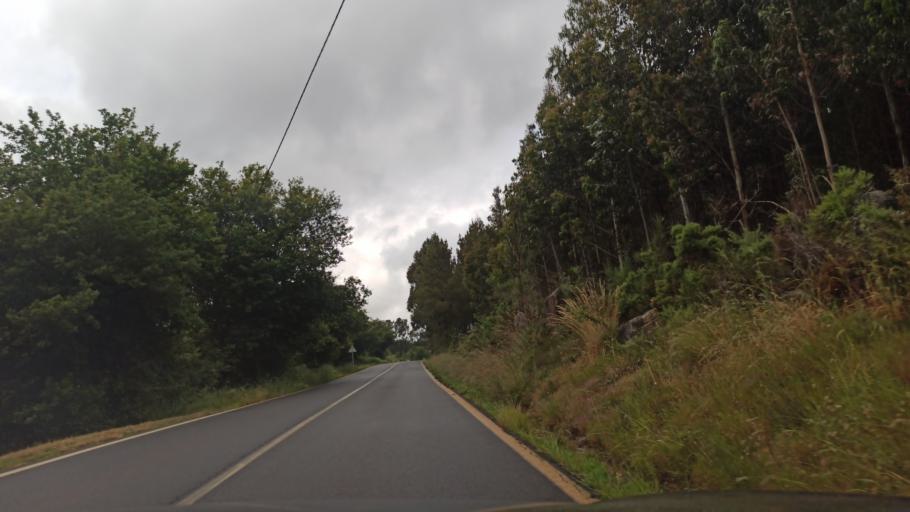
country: ES
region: Galicia
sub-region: Provincia da Coruna
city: Santiso
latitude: 42.7768
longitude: -8.0360
